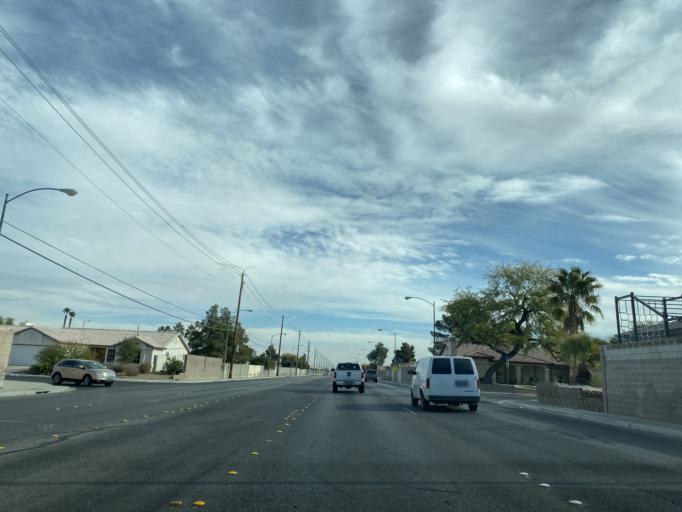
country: US
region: Nevada
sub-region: Clark County
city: Las Vegas
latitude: 36.2467
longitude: -115.2018
